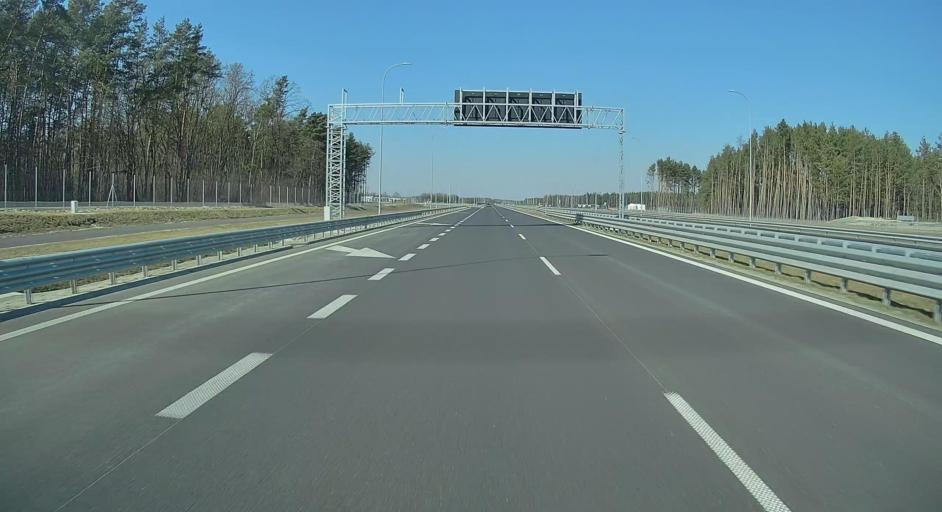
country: PL
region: Subcarpathian Voivodeship
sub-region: Powiat nizanski
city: Jezowe
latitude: 50.3843
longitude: 22.1630
